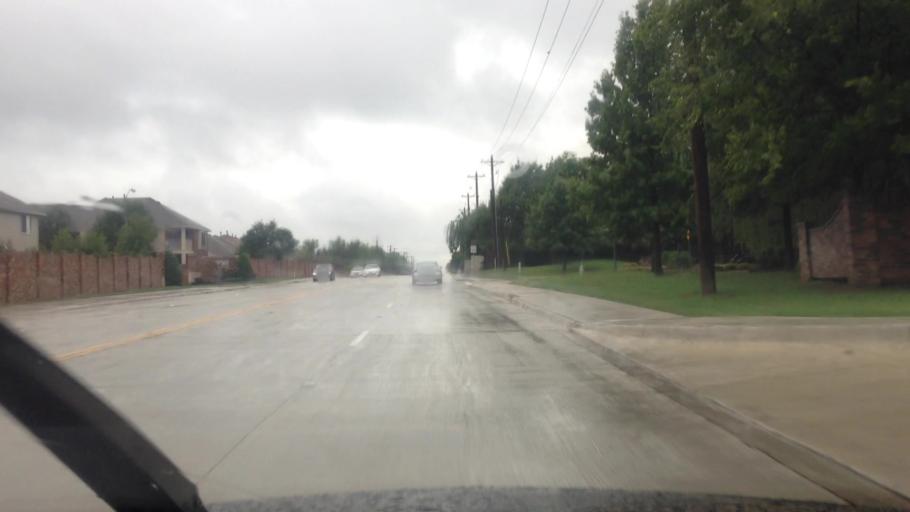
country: US
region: Texas
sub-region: Tarrant County
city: Watauga
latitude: 32.8925
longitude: -97.2404
